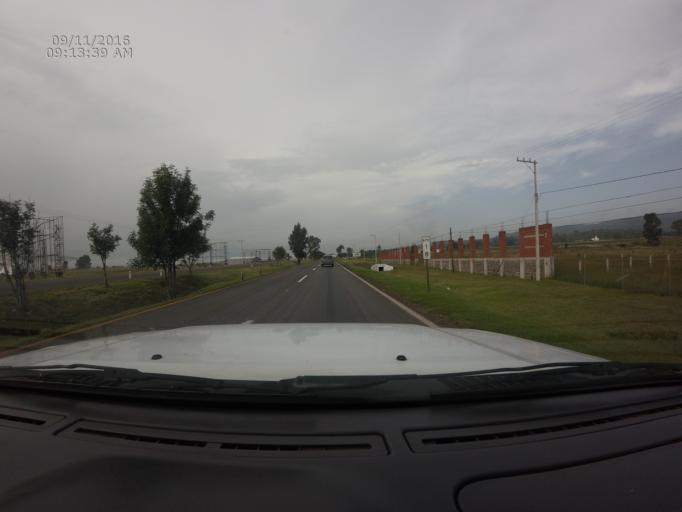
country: MX
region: Michoacan
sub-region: Morelia
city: La Mintzita (Piedra Dura)
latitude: 19.5803
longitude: -101.3102
